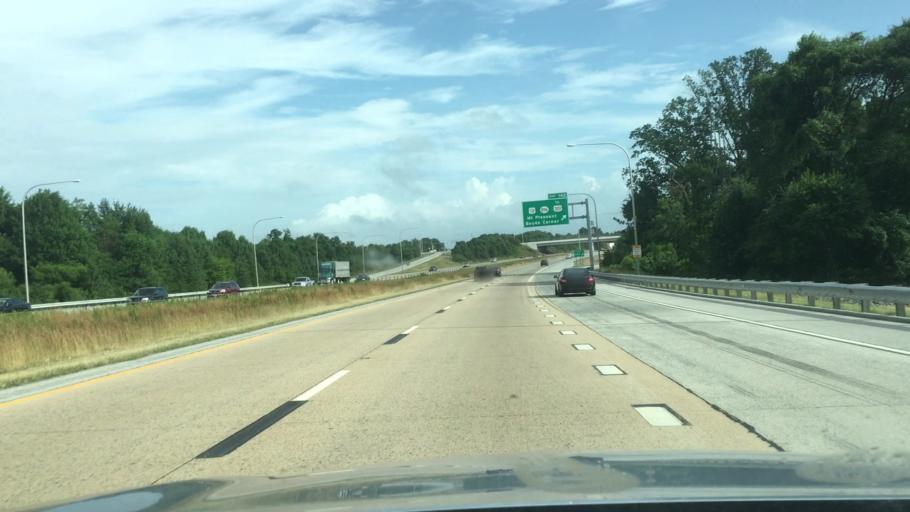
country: US
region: Delaware
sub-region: New Castle County
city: Middletown
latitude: 39.5056
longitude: -75.6468
